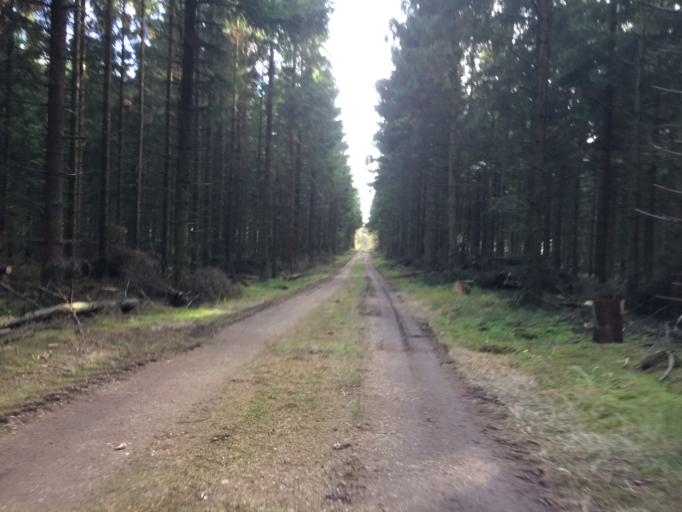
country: DK
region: Central Jutland
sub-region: Holstebro Kommune
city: Ulfborg
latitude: 56.2077
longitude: 8.4667
